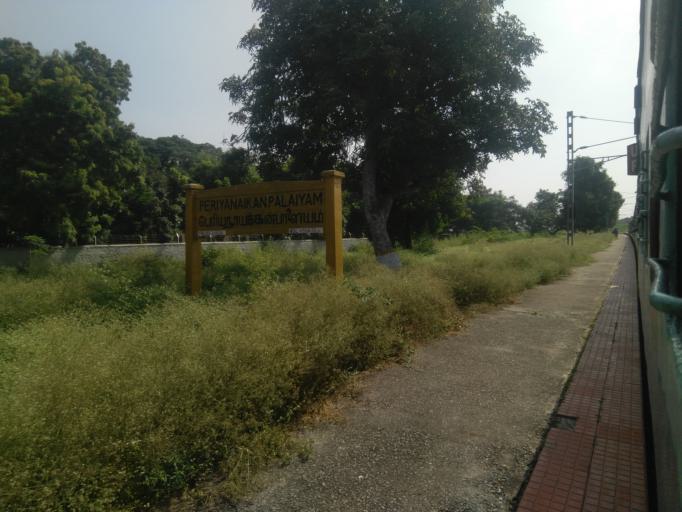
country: IN
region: Tamil Nadu
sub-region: Coimbatore
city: Periyanayakkanpalaiyam
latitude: 11.1459
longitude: 76.9491
